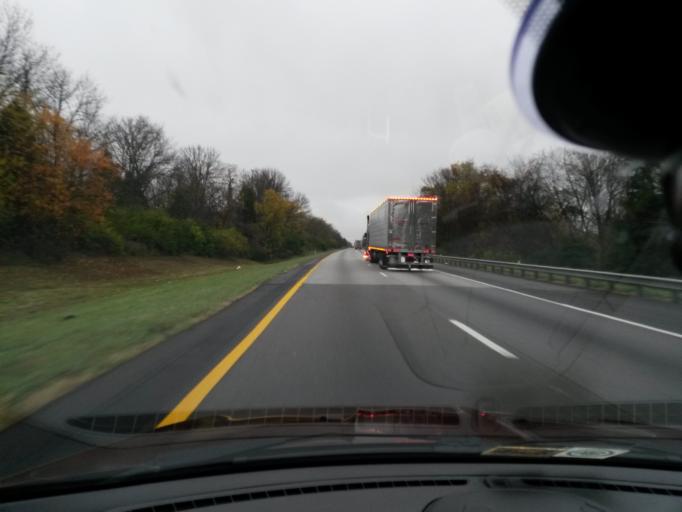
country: US
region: Virginia
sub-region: Botetourt County
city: Daleville
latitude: 37.4049
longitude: -79.8949
